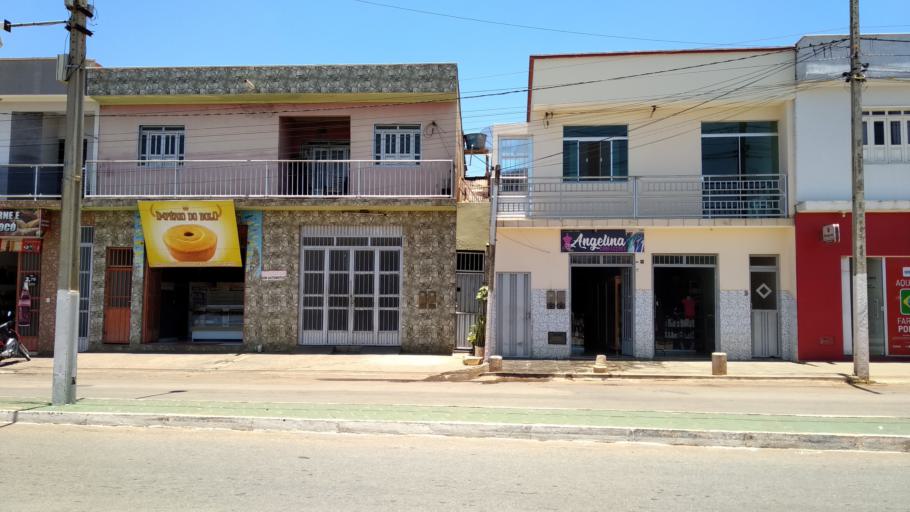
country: BR
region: Bahia
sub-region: Caetite
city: Caetite
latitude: -14.0612
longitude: -42.4839
